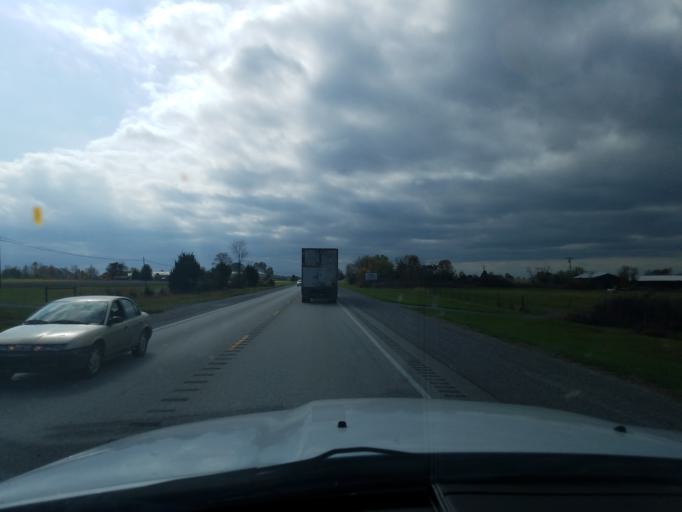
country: US
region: Kentucky
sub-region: Taylor County
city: Campbellsville
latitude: 37.3773
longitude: -85.2984
